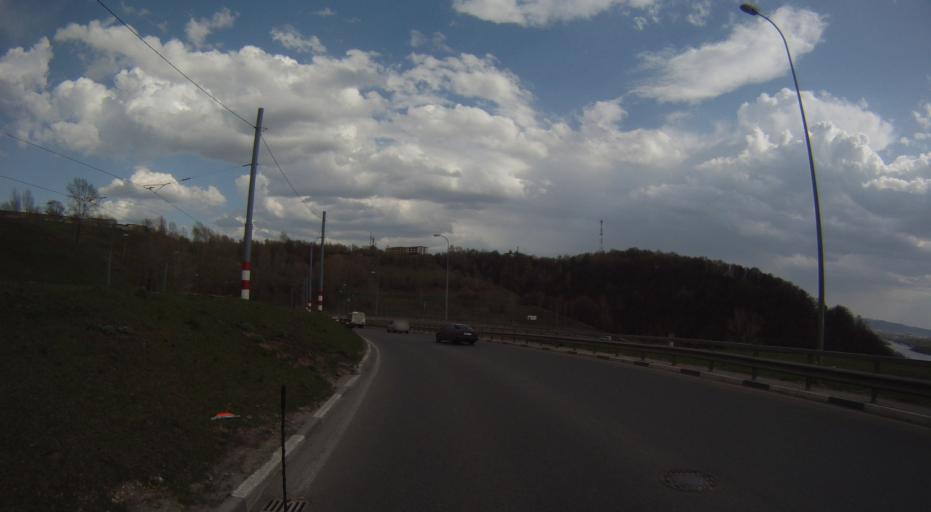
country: RU
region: Nizjnij Novgorod
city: Nizhniy Novgorod
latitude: 56.3008
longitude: 43.9703
